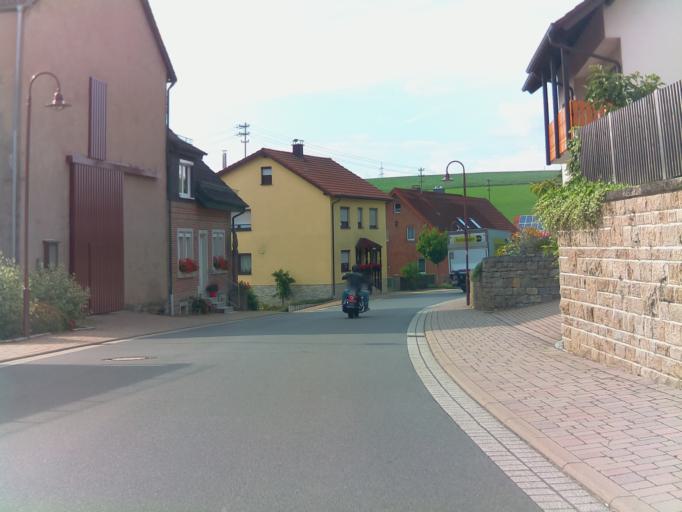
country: DE
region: Baden-Wuerttemberg
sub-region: Karlsruhe Region
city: Rosenberg
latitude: 49.5223
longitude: 9.4402
